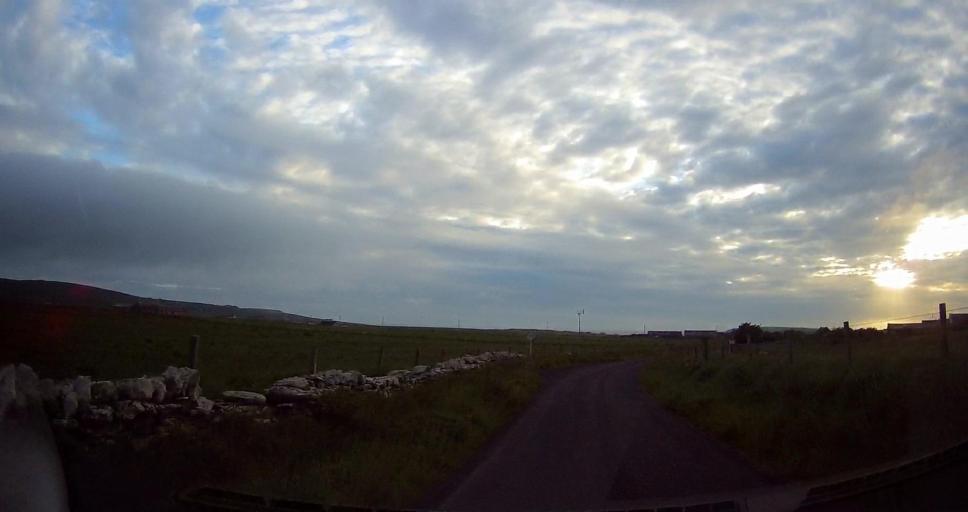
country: GB
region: Scotland
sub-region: Orkney Islands
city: Stromness
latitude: 59.1258
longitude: -3.2852
